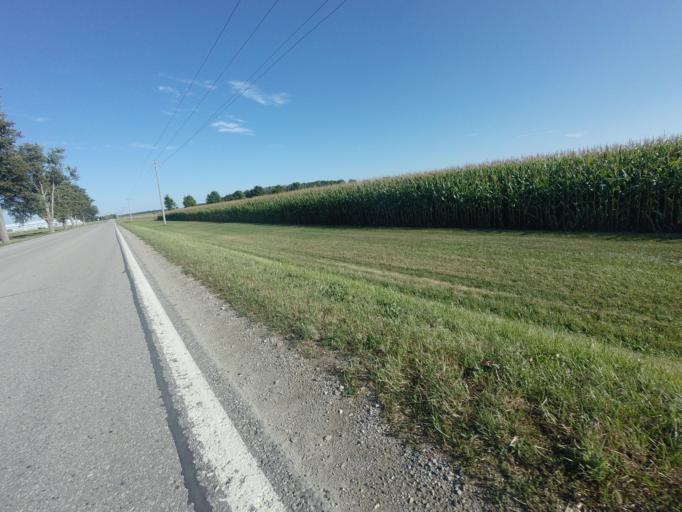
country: CA
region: Ontario
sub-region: Wellington County
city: Guelph
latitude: 43.6425
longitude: -80.4044
